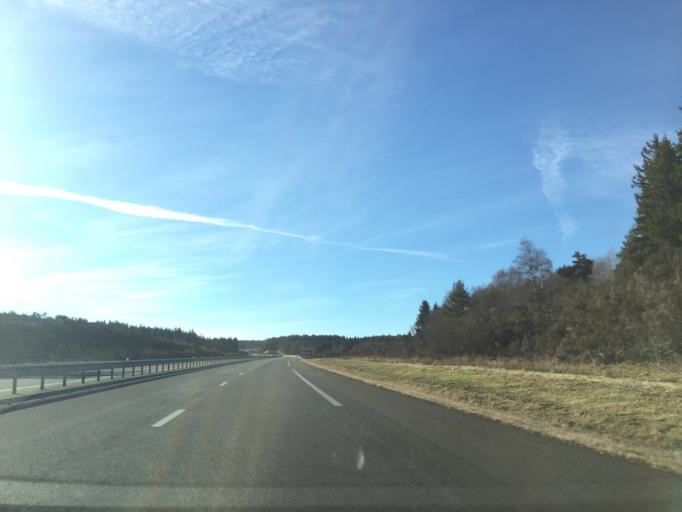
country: FR
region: Auvergne
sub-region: Departement du Puy-de-Dome
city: Gelles
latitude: 45.7540
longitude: 2.7233
